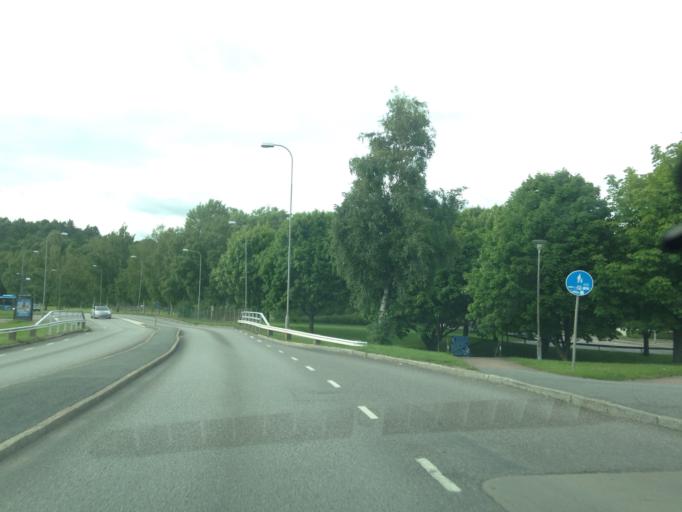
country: SE
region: Vaestra Goetaland
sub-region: Goteborg
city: Goeteborg
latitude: 57.7538
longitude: 11.9810
